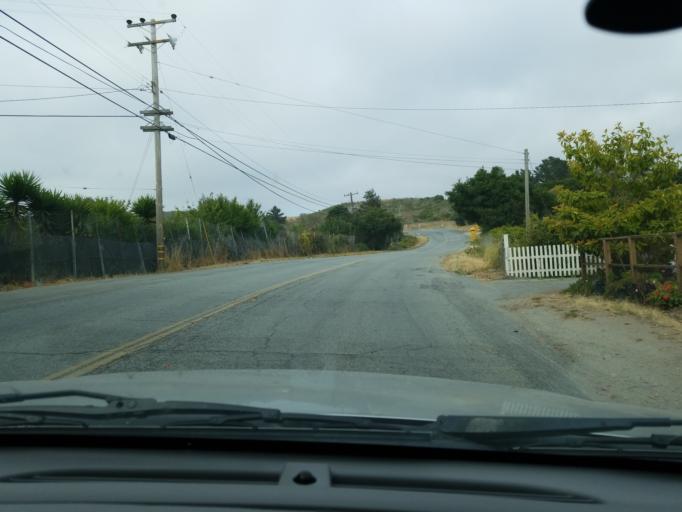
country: US
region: California
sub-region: Monterey County
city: Las Lomas
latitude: 36.8676
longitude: -121.7464
